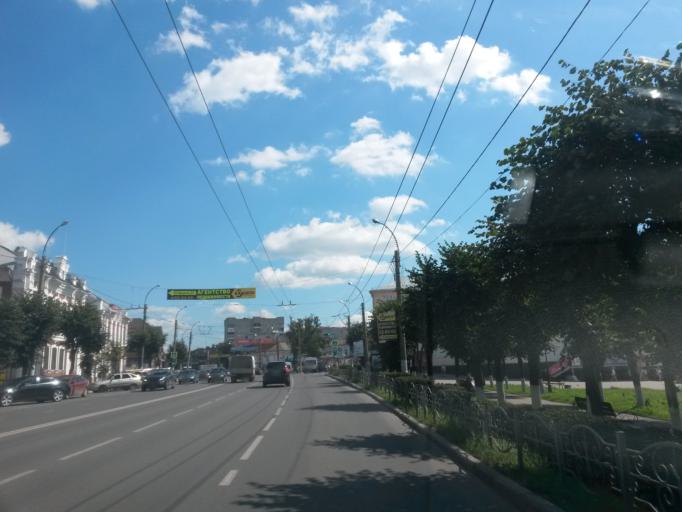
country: RU
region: Ivanovo
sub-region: Gorod Ivanovo
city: Ivanovo
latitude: 56.9958
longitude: 40.9824
